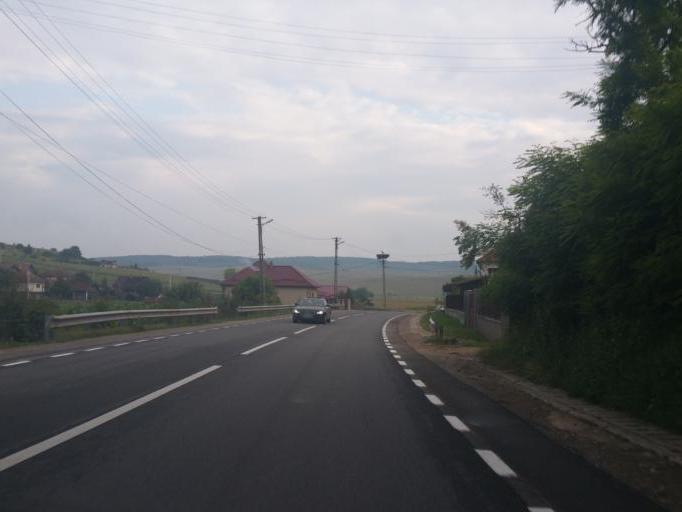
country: RO
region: Cluj
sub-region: Comuna Sanpaul
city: Sanpaul
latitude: 46.9004
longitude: 23.4149
